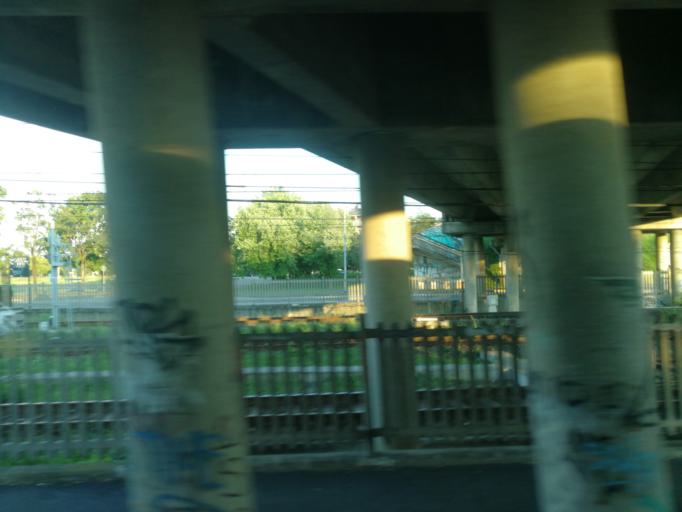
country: IT
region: Lombardy
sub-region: Citta metropolitana di Milano
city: Cologno Monzese
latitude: 45.5334
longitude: 9.2897
